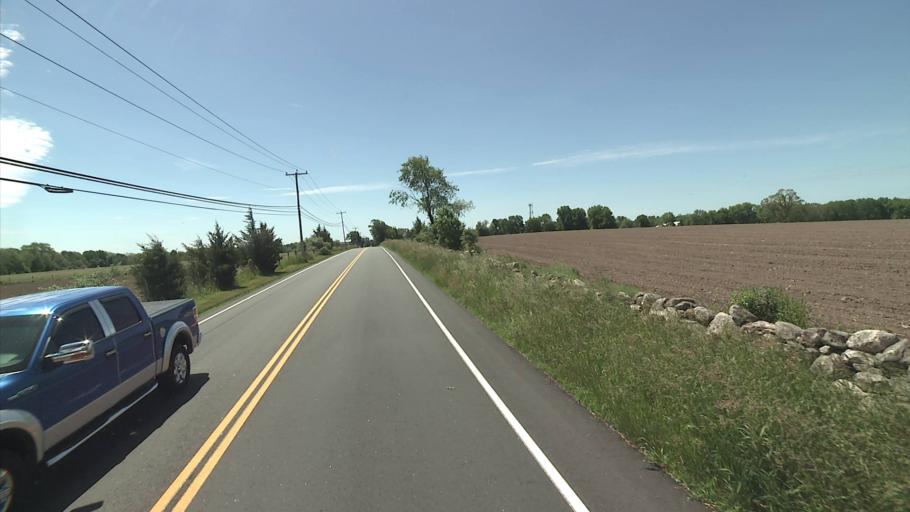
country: US
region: Connecticut
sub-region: Windham County
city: Moosup
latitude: 41.6700
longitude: -71.8486
